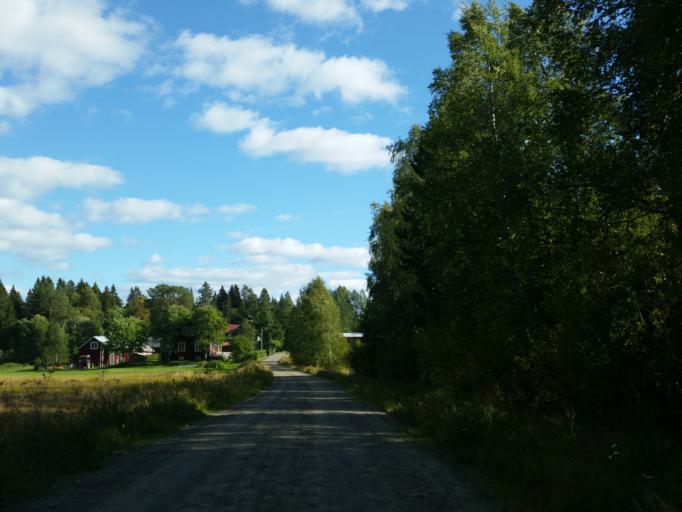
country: SE
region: Vaesterbotten
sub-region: Robertsfors Kommun
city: Robertsfors
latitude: 64.1615
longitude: 20.9544
